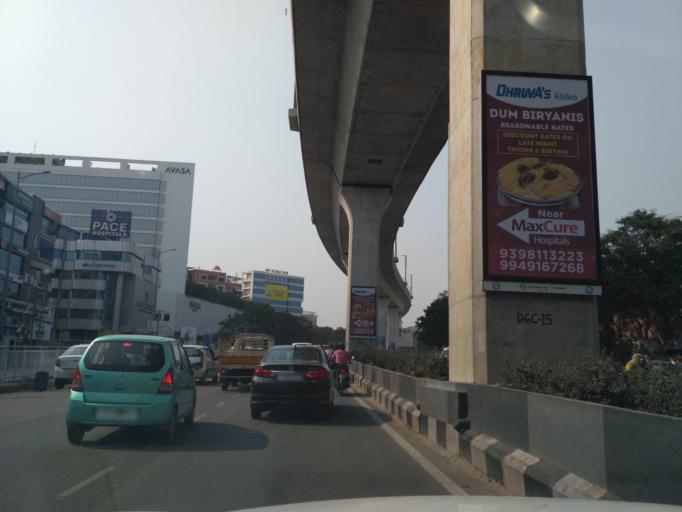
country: IN
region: Telangana
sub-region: Rangareddi
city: Kukatpalli
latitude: 17.4463
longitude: 78.3851
